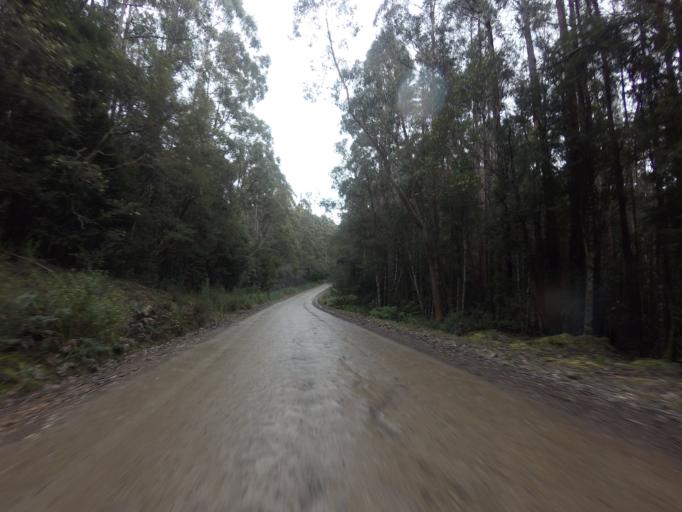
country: AU
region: Tasmania
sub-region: Huon Valley
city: Geeveston
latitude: -43.4817
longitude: 146.8919
